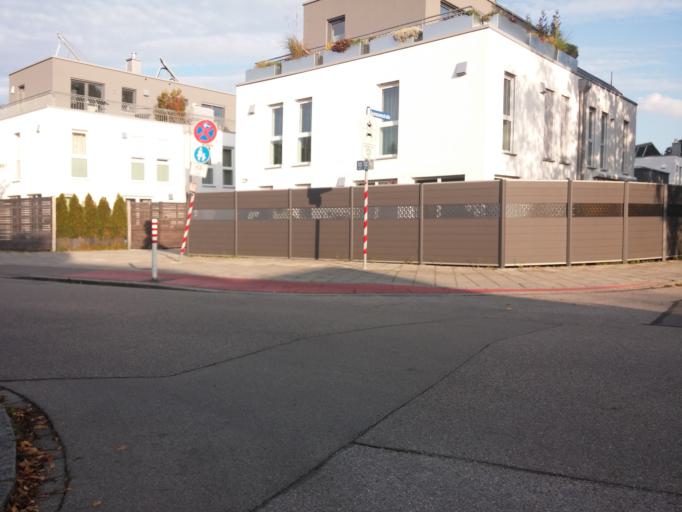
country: DE
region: Bavaria
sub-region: Upper Bavaria
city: Vaterstetten
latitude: 48.1029
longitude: 11.7635
